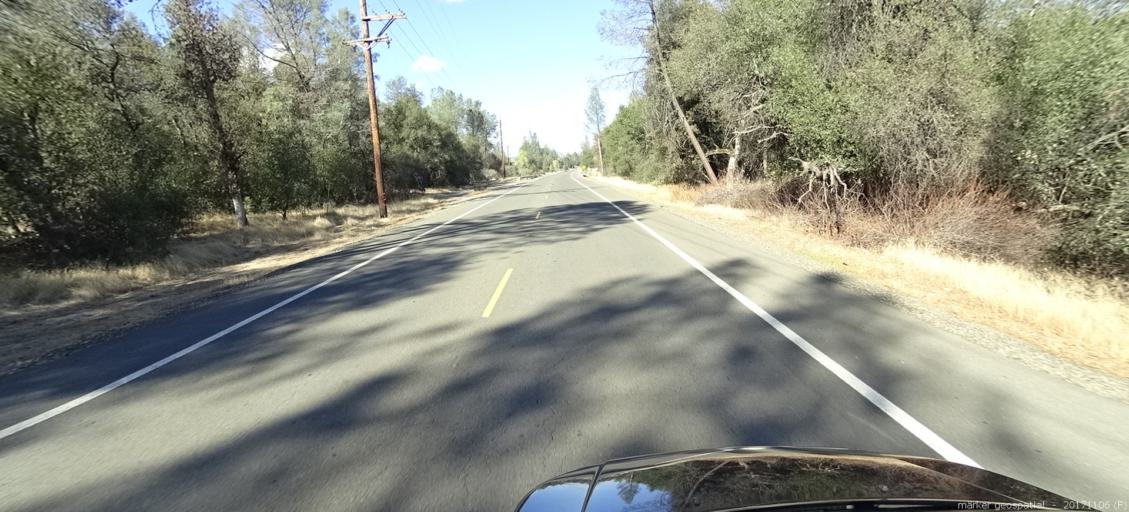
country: US
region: California
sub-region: Shasta County
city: Redding
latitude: 40.6024
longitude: -122.3140
